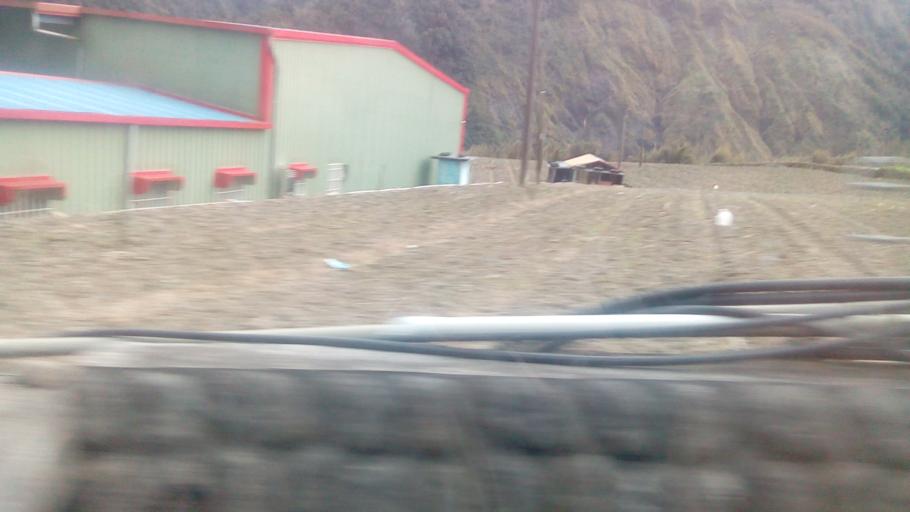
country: TW
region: Taiwan
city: Daxi
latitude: 24.4680
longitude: 121.4055
